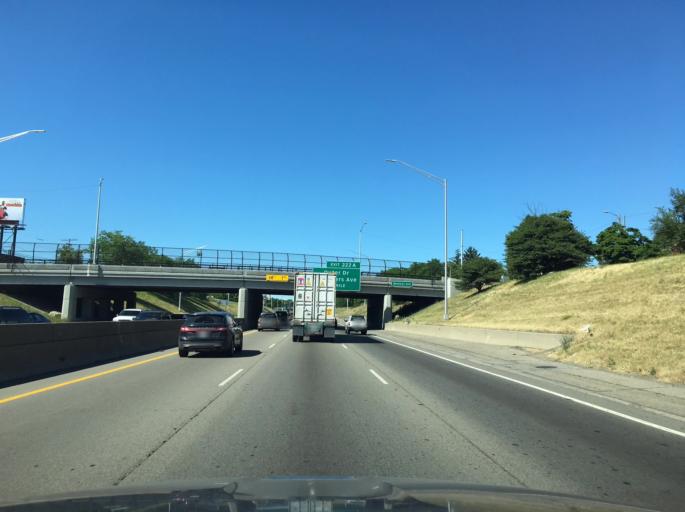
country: US
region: Michigan
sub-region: Wayne County
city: Harper Woods
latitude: 42.4135
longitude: -82.9427
